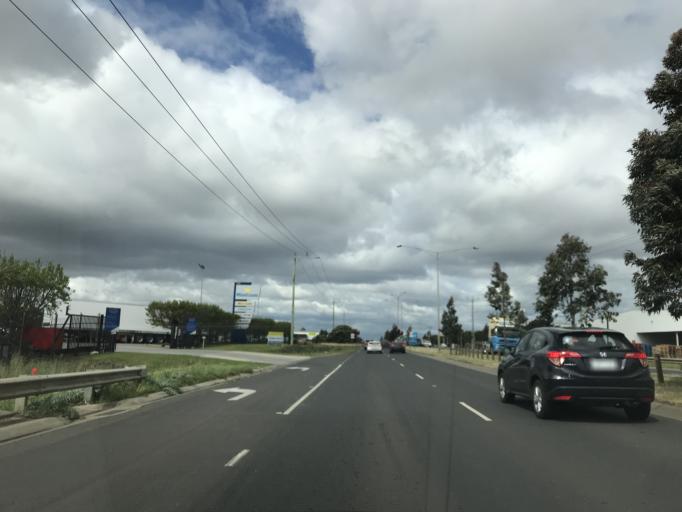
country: AU
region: Victoria
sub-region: Brimbank
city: Derrimut
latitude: -37.8124
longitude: 144.7742
